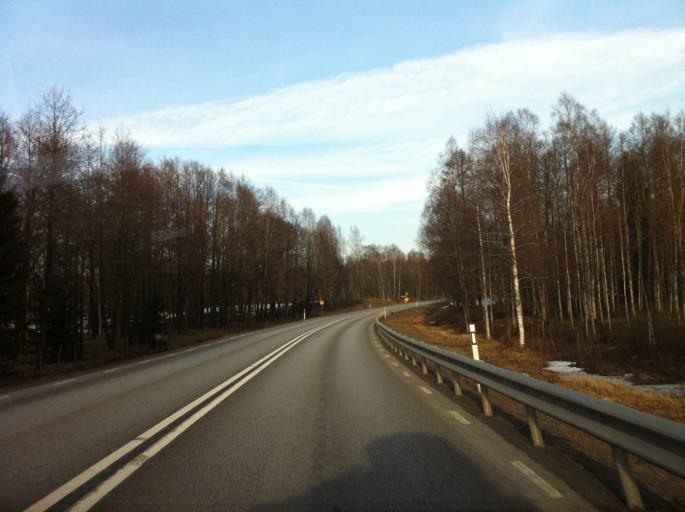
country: SE
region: Vaermland
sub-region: Filipstads Kommun
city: Filipstad
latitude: 59.7519
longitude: 14.2414
